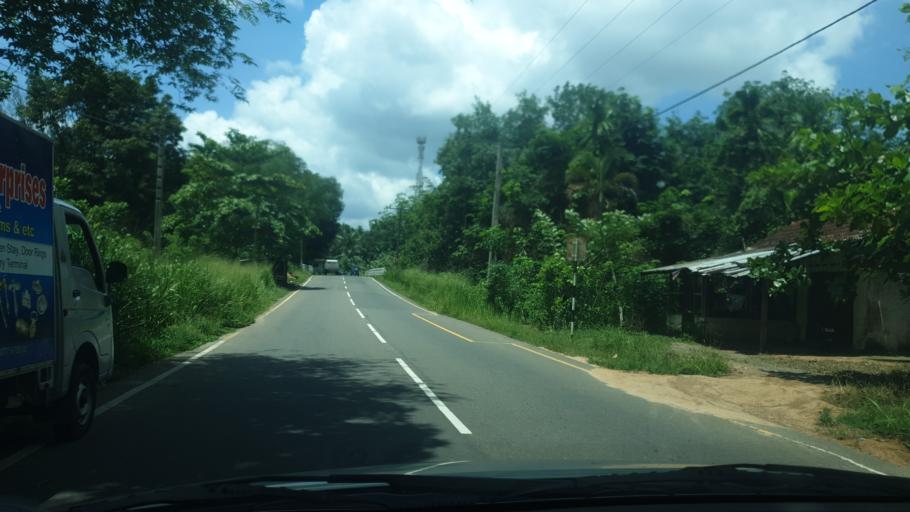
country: LK
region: Western
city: Horawala Junction
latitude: 6.5141
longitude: 80.2432
